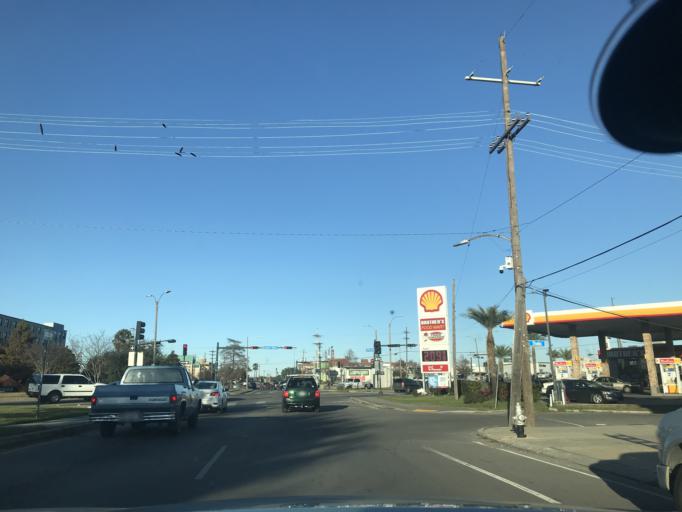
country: US
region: Louisiana
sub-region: Orleans Parish
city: New Orleans
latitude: 29.9564
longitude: -90.1051
